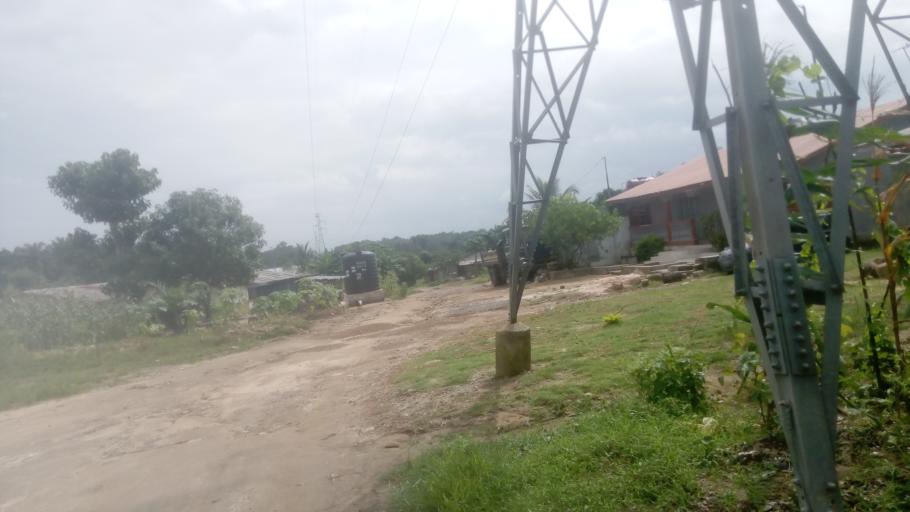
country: SL
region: Northern Province
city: Lunsar
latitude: 8.6928
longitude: -12.5390
